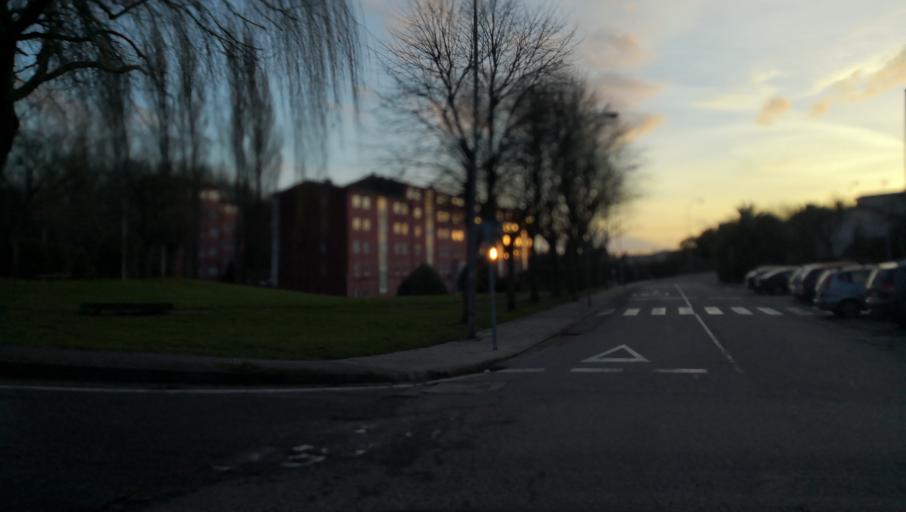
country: ES
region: Galicia
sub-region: Provincia da Coruna
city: Santiago de Compostela
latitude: 42.8921
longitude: -8.5346
